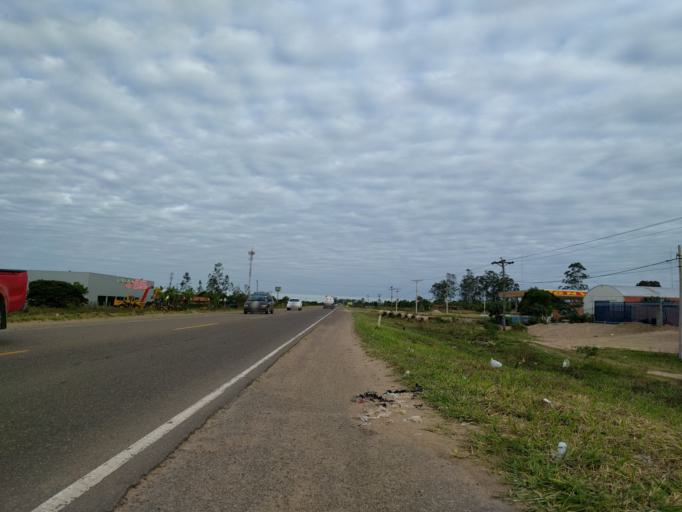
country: BO
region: Santa Cruz
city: Santa Rita
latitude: -17.8820
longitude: -63.2663
